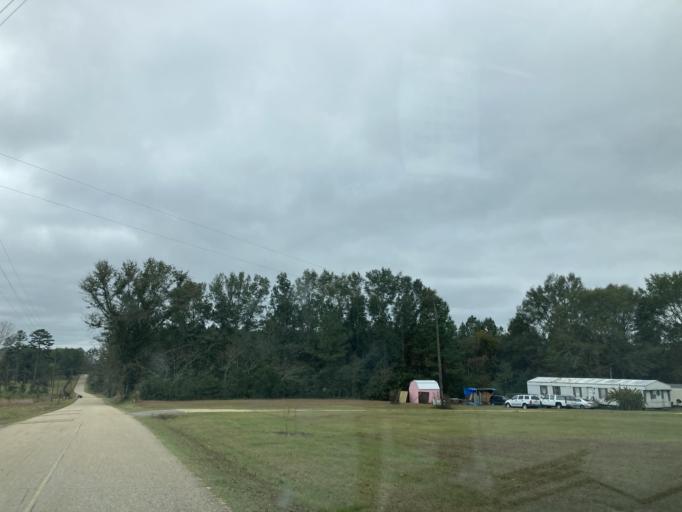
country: US
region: Mississippi
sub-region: Lamar County
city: West Hattiesburg
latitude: 31.2687
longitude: -89.5059
